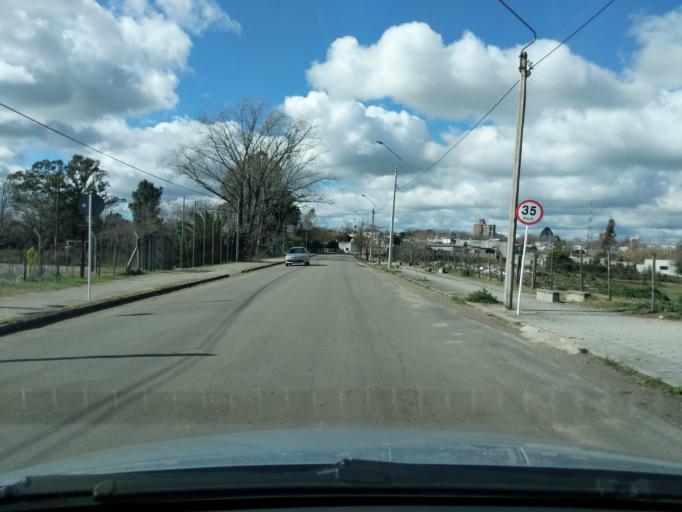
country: UY
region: Florida
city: Florida
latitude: -34.0913
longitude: -56.2252
